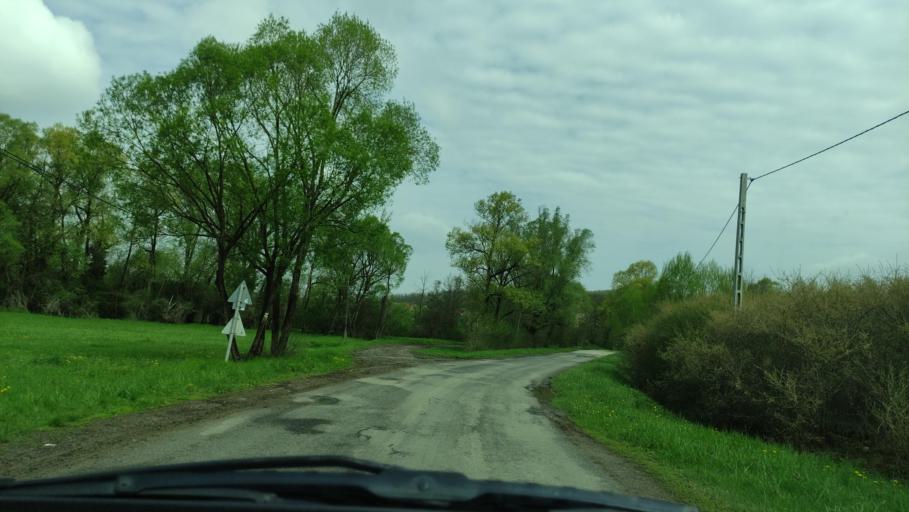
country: HU
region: Baranya
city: Magocs
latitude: 46.2712
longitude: 18.2157
